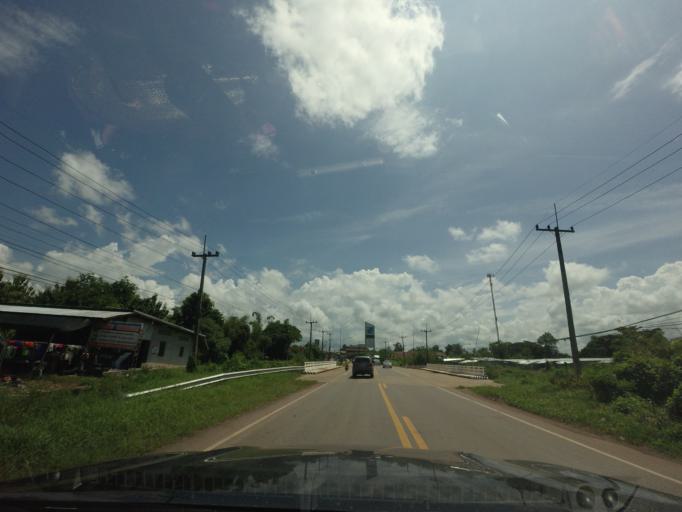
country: TH
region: Changwat Udon Thani
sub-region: Amphoe Ban Phue
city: Ban Phue
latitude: 17.6963
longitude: 102.4539
